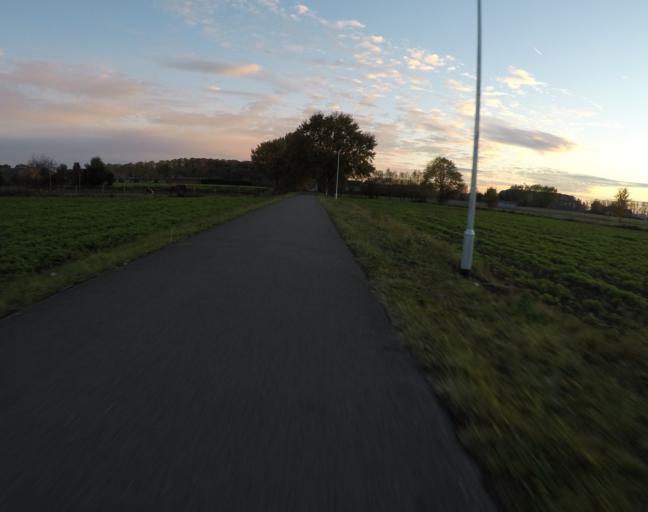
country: BE
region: Flanders
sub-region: Provincie Antwerpen
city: Herentals
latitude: 51.1496
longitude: 4.8211
